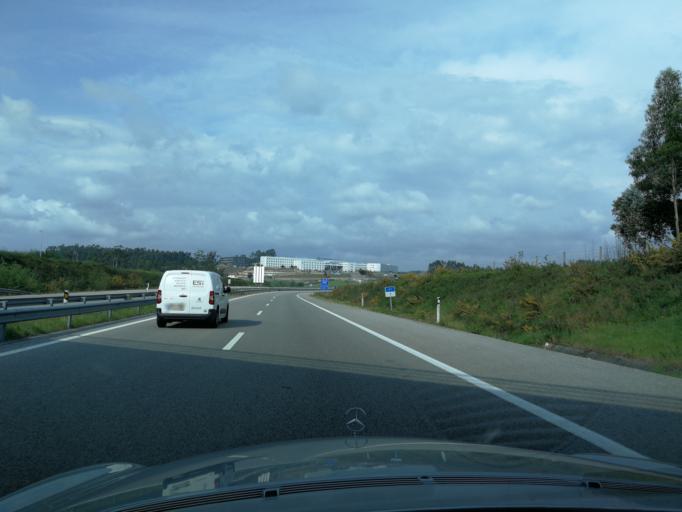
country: PT
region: Porto
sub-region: Vila do Conde
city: Vila do Conde
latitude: 41.3799
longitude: -8.7169
